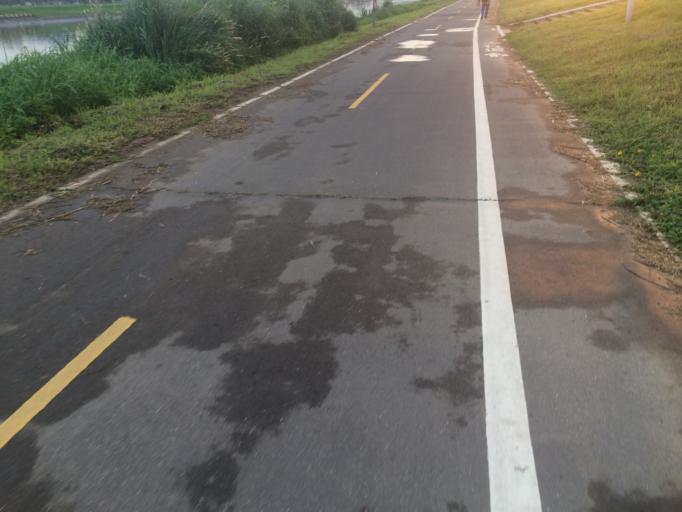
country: TW
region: Taipei
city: Taipei
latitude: 25.0767
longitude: 121.5511
